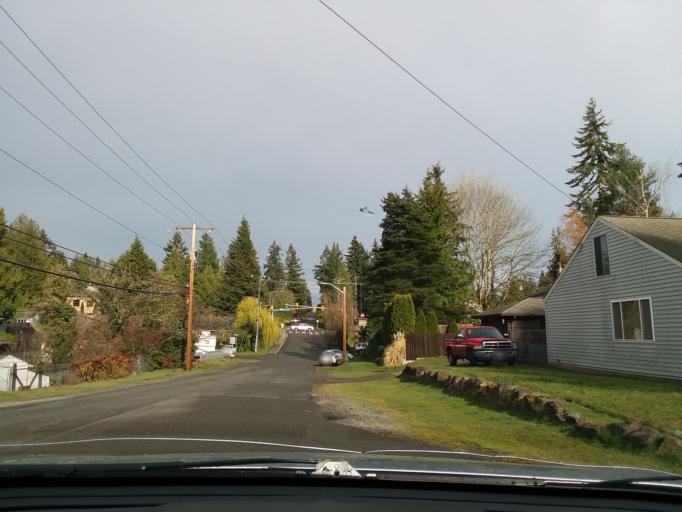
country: US
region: Washington
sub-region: King County
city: Shoreline
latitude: 47.7521
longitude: -122.3153
